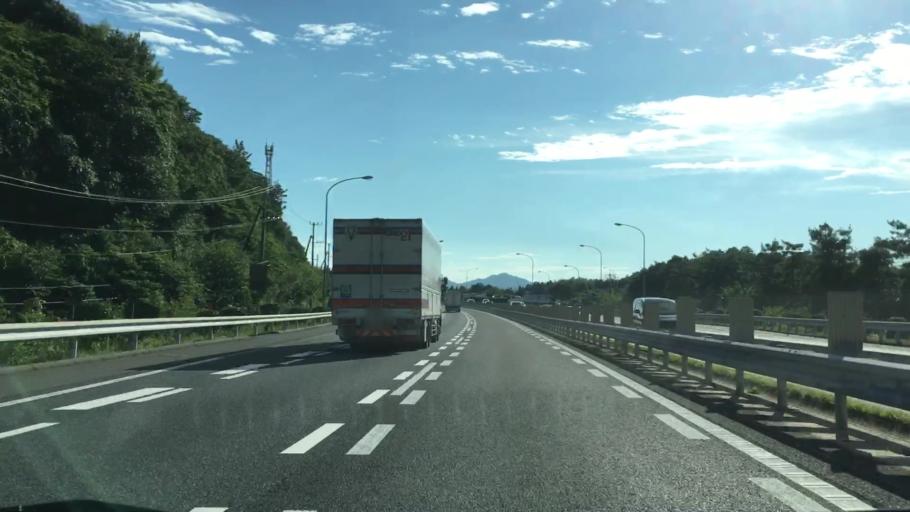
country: JP
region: Yamaguchi
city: Iwakuni
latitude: 34.1014
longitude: 132.1051
